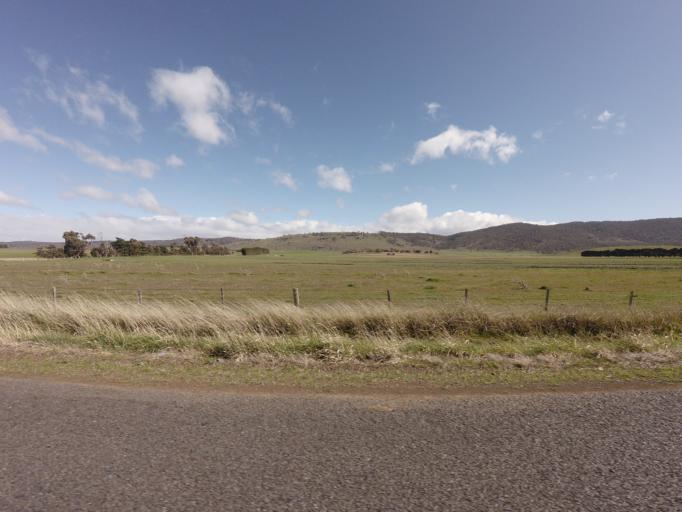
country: AU
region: Tasmania
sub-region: Northern Midlands
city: Evandale
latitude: -41.9921
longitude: 147.4530
